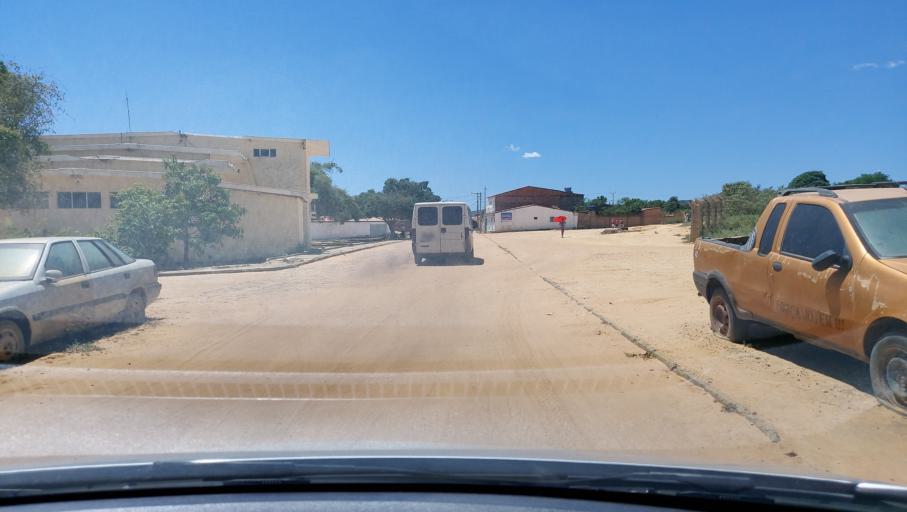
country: BR
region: Bahia
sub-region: Oliveira Dos Brejinhos
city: Beira Rio
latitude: -12.0007
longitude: -42.6295
